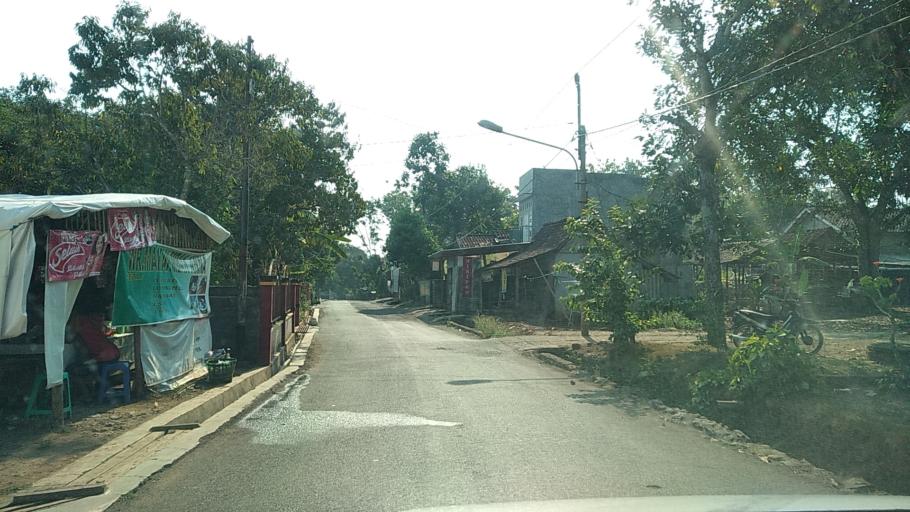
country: ID
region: Central Java
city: Semarang
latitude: -7.0193
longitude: 110.3113
